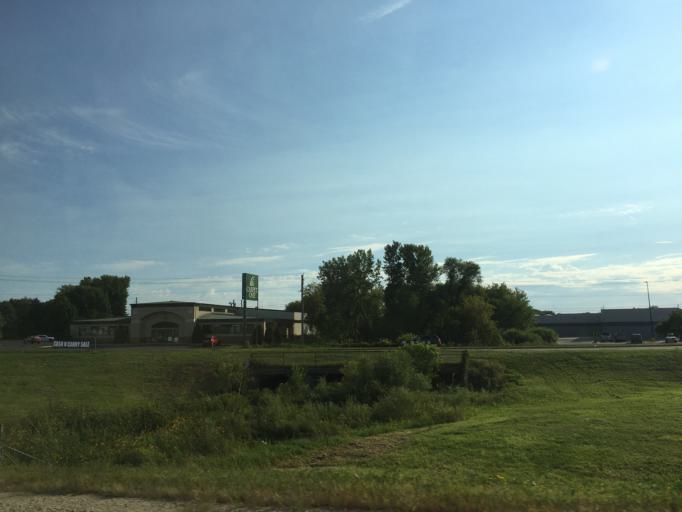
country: US
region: Minnesota
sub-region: Olmsted County
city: Rochester
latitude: 44.0784
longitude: -92.5087
